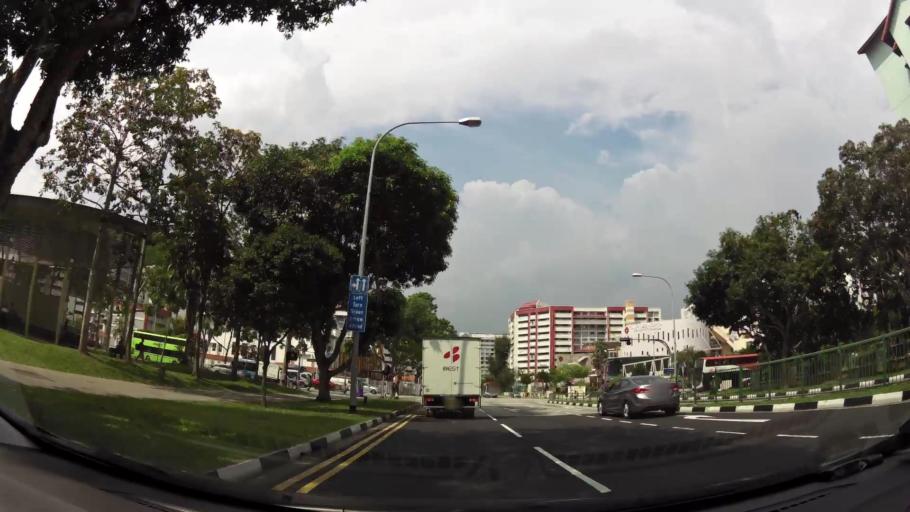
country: SG
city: Singapore
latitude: 1.3563
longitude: 103.9462
